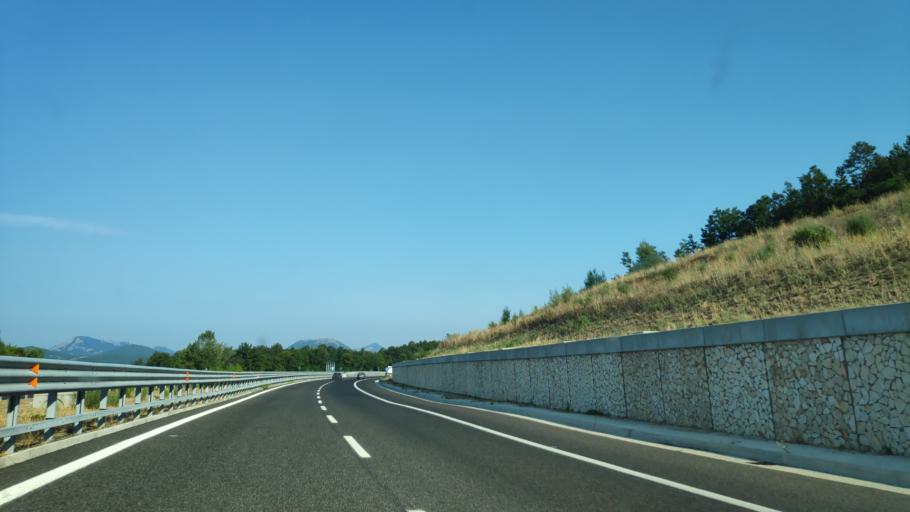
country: IT
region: Basilicate
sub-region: Provincia di Potenza
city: Nemoli
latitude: 40.1022
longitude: 15.7990
